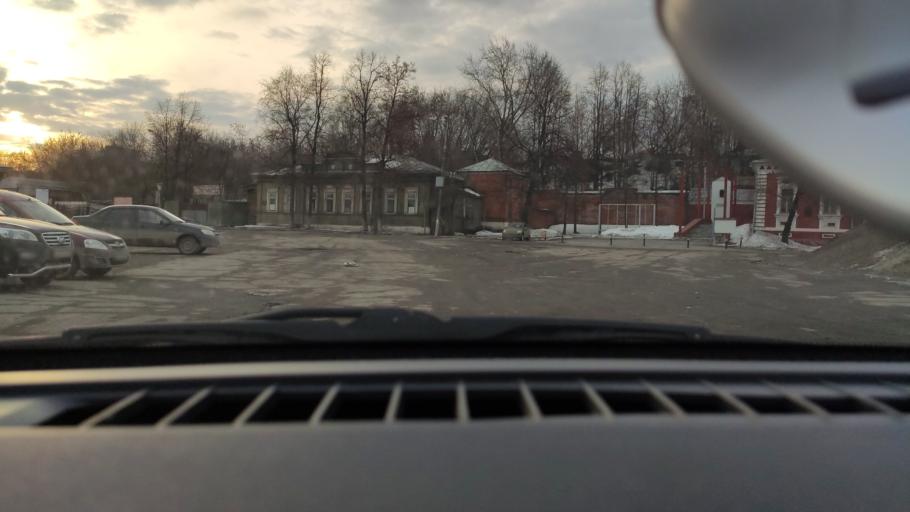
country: RU
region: Perm
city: Perm
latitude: 58.0354
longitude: 56.3082
